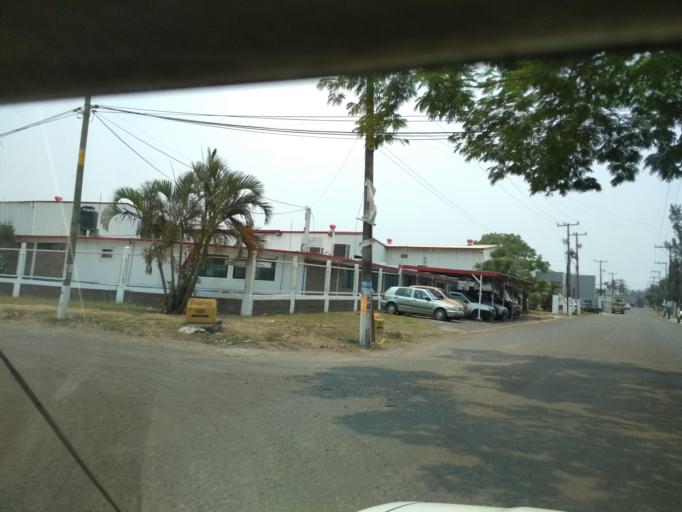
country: MX
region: Veracruz
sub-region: Veracruz
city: Lomas de Rio Medio Cuatro
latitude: 19.1660
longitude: -96.2404
